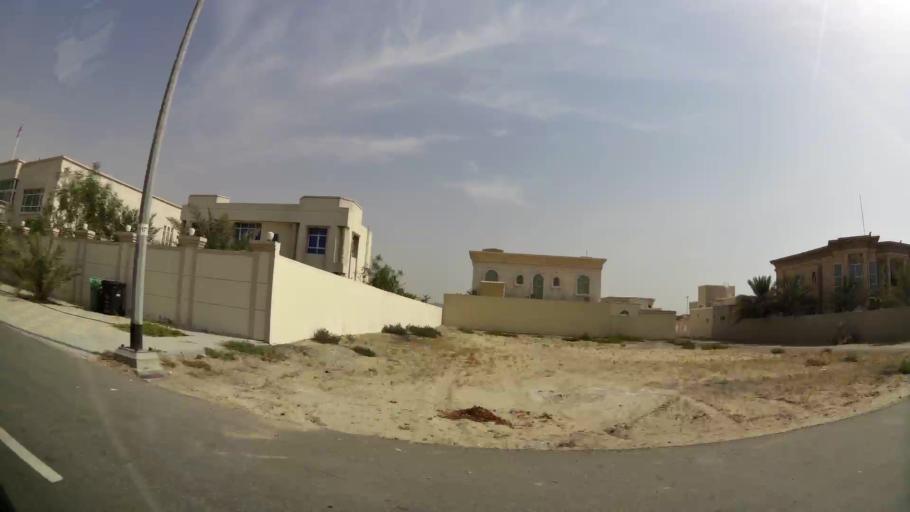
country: AE
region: Ash Shariqah
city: Sharjah
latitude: 25.2479
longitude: 55.4339
